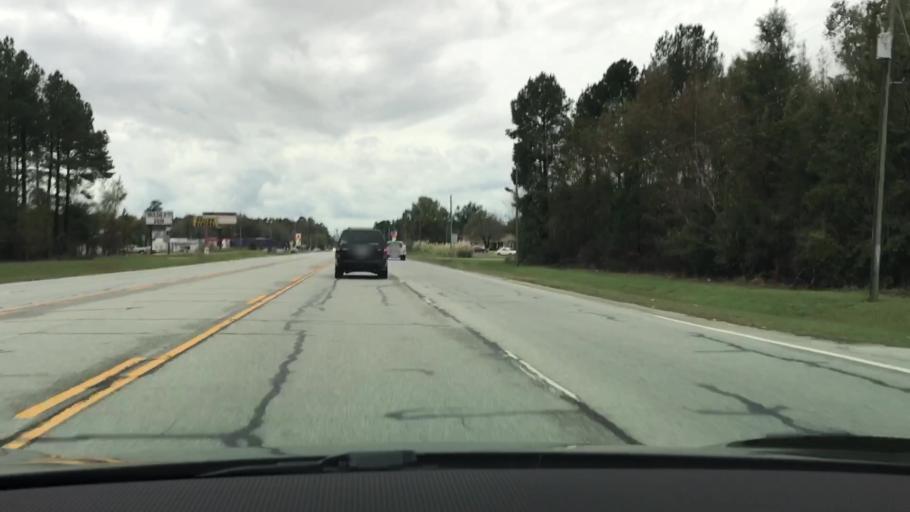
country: US
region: Georgia
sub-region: Jefferson County
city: Wadley
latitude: 32.8720
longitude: -82.3958
